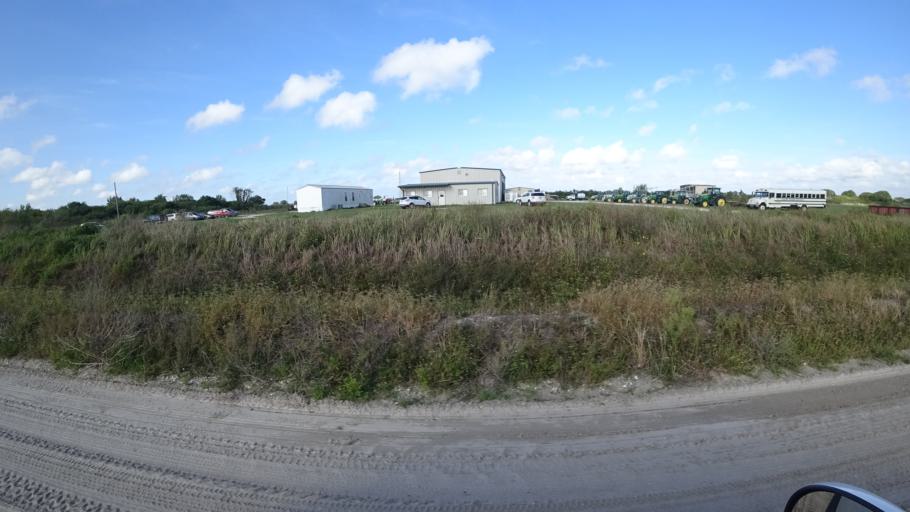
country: US
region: Florida
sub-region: Hillsborough County
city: Wimauma
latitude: 27.5428
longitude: -82.3207
